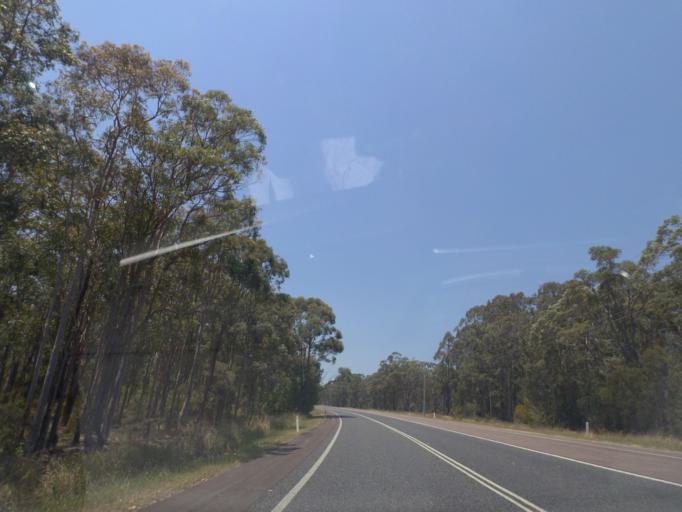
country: AU
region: New South Wales
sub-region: Port Stephens Shire
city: Port Stephens
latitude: -32.6387
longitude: 152.0226
